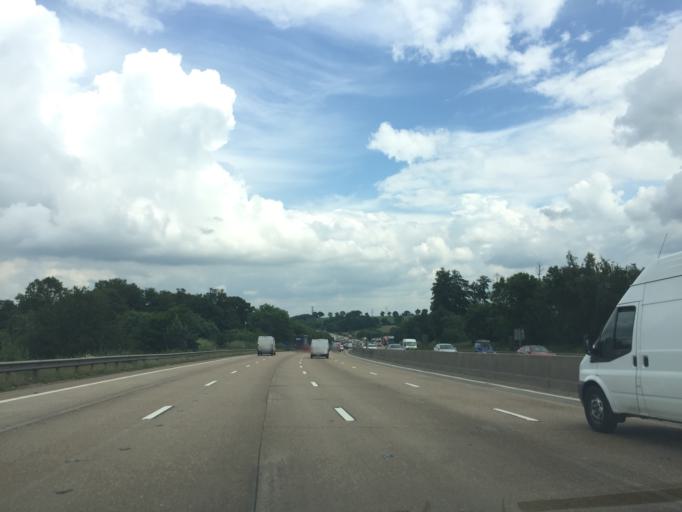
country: GB
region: England
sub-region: Hertfordshire
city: Cuffley
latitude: 51.6916
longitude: -0.1047
